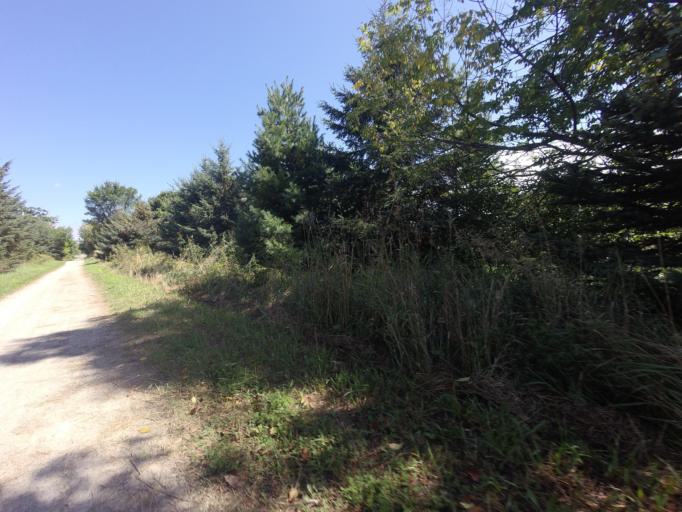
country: CA
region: Ontario
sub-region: Wellington County
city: Guelph
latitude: 43.7284
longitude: -80.3699
